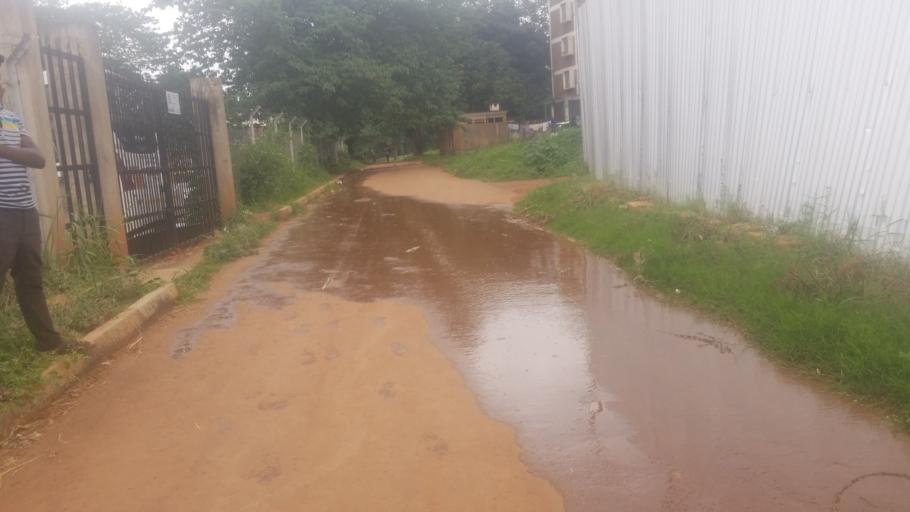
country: UG
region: Central Region
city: Kampala Central Division
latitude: 0.3344
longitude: 32.5708
